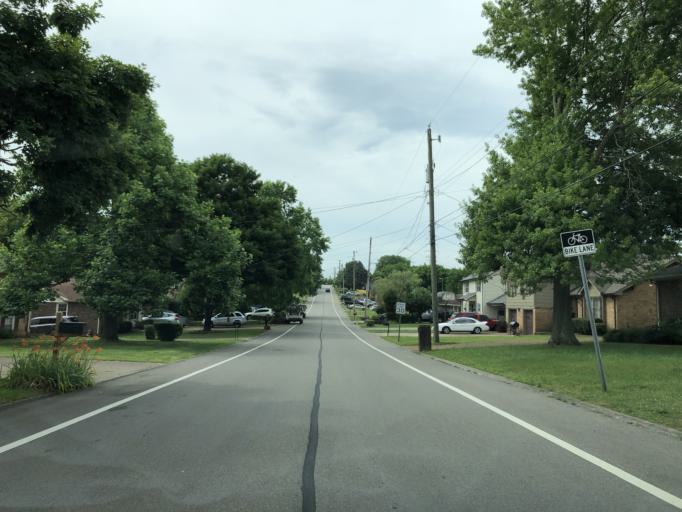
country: US
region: Tennessee
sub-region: Davidson County
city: Goodlettsville
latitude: 36.2846
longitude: -86.7151
